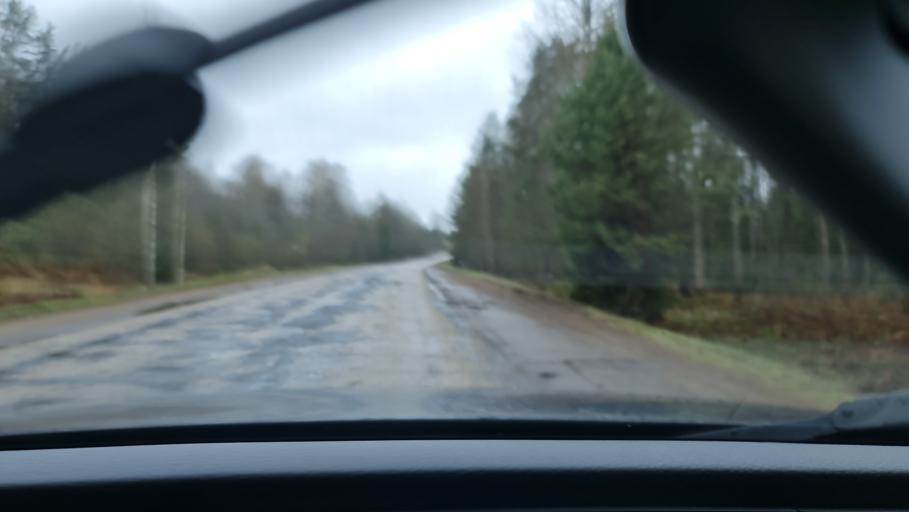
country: RU
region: Novgorod
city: Valday
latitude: 58.0362
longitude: 32.8889
